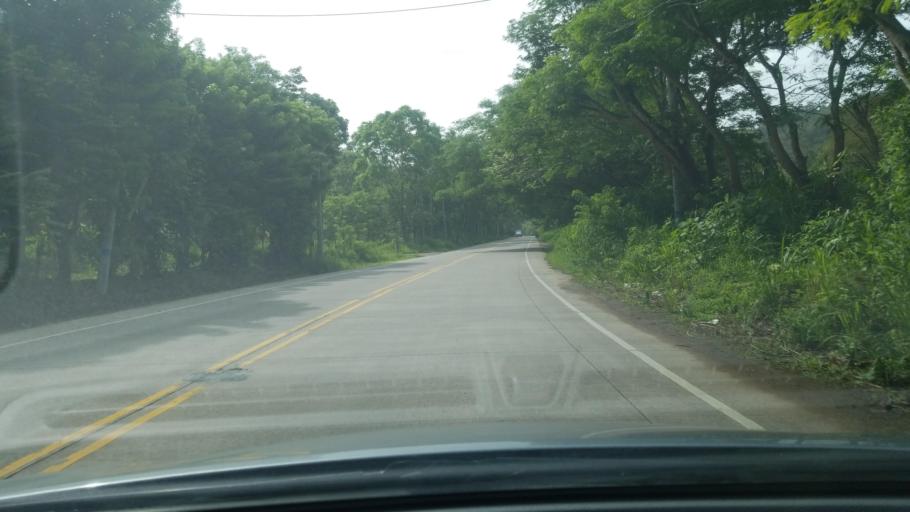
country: HN
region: Copan
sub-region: Santa Rita
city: Santa Rita, Copan
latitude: 14.8712
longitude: -89.0778
